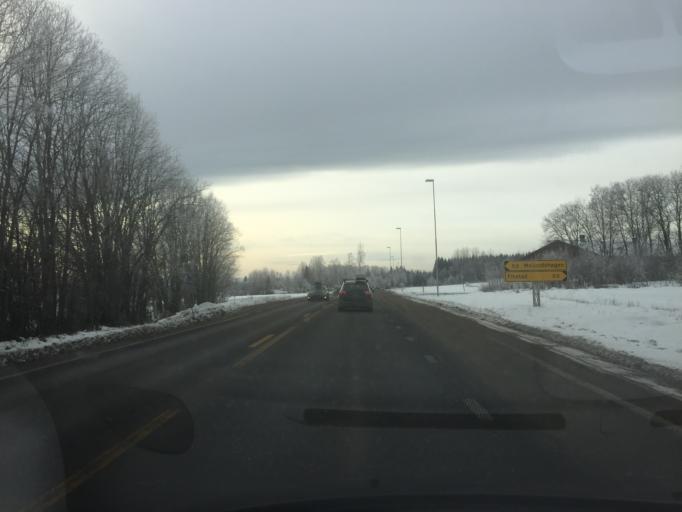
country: NO
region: Hedmark
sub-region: Elverum
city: Elverum
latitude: 60.9269
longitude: 11.6687
